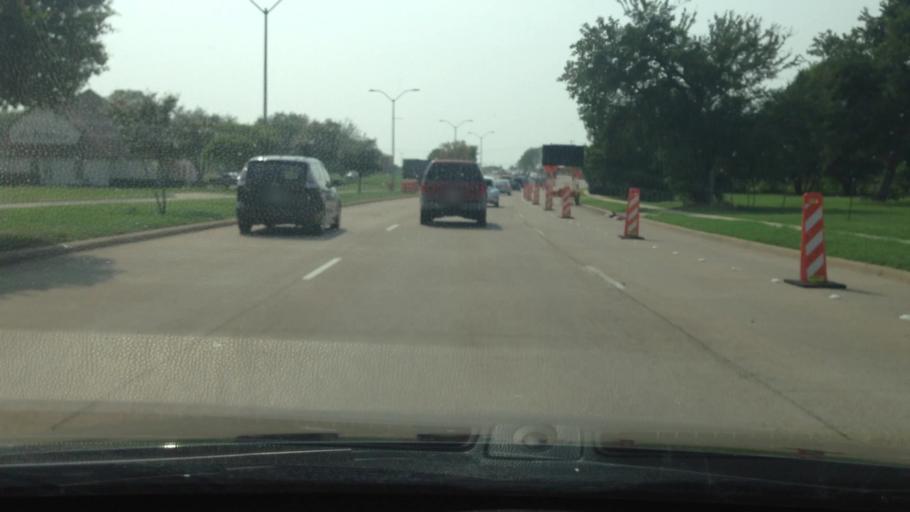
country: US
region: Texas
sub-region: Tarrant County
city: North Richland Hills
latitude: 32.8618
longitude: -97.2044
